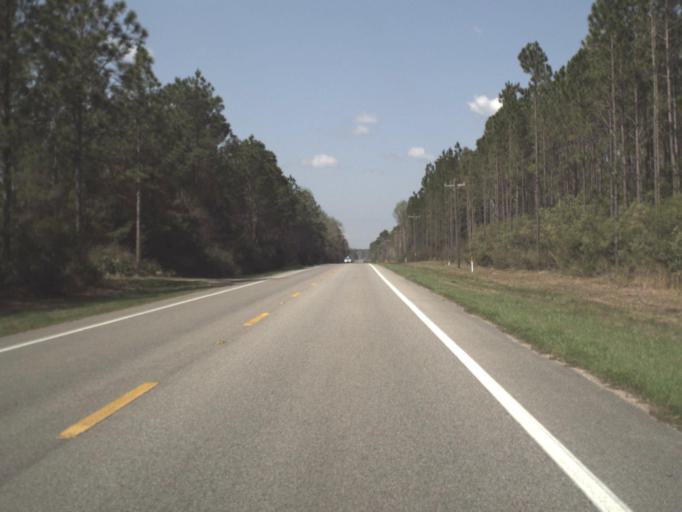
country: US
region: Florida
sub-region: Liberty County
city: Bristol
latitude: 30.3866
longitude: -84.7680
